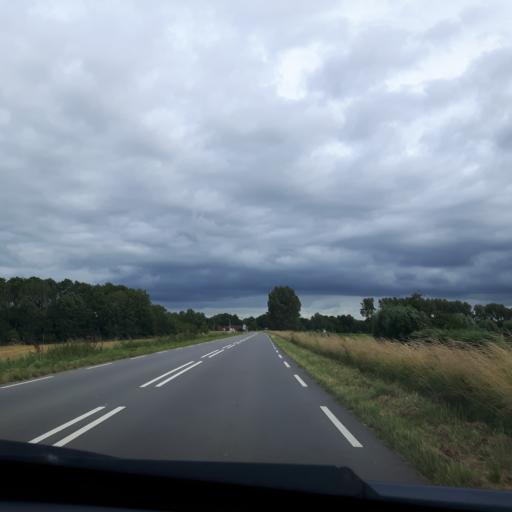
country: NL
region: Zeeland
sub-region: Gemeente Goes
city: Goes
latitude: 51.5598
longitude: 3.8068
